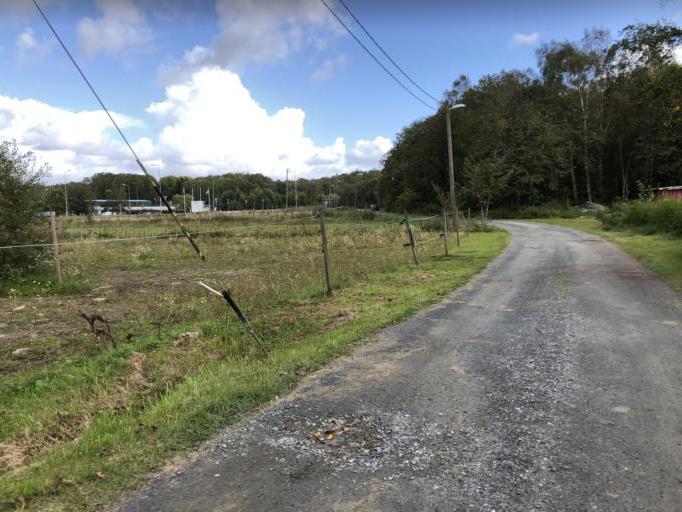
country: SE
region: Vaestra Goetaland
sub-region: Goteborg
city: Majorna
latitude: 57.7475
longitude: 11.8782
